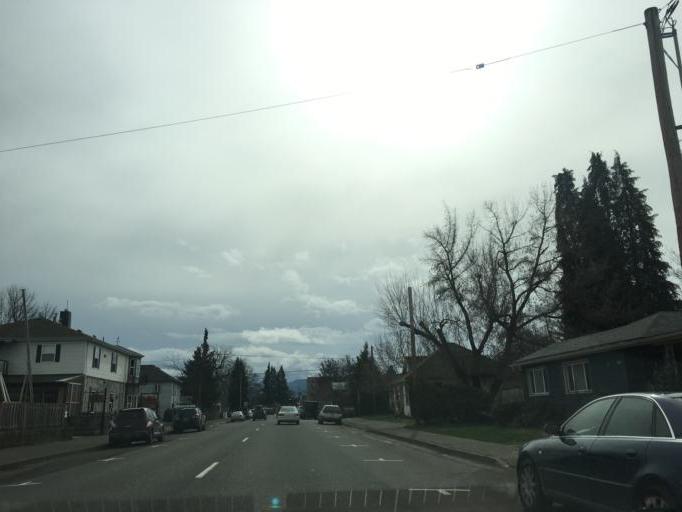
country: US
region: Oregon
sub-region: Hood River County
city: Hood River
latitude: 45.7023
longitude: -121.5247
